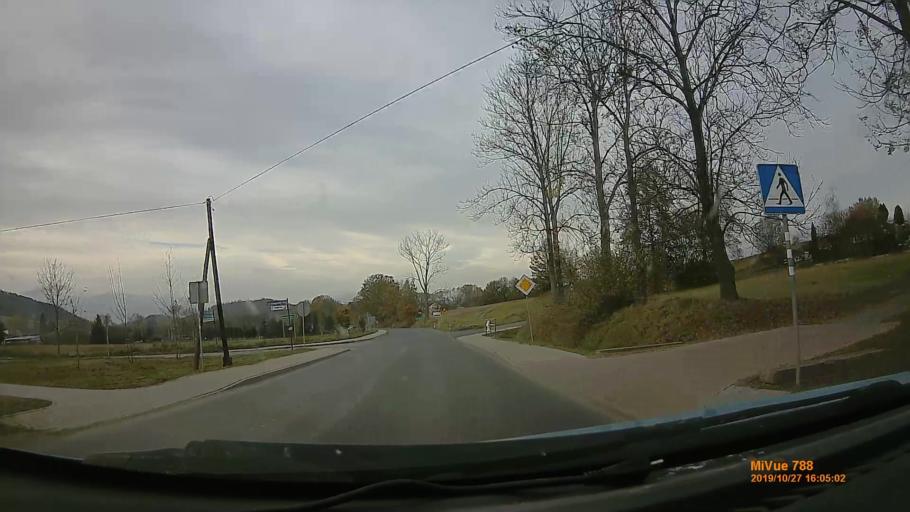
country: PL
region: Lower Silesian Voivodeship
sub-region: Powiat klodzki
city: Nowa Ruda
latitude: 50.5279
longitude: 16.4845
